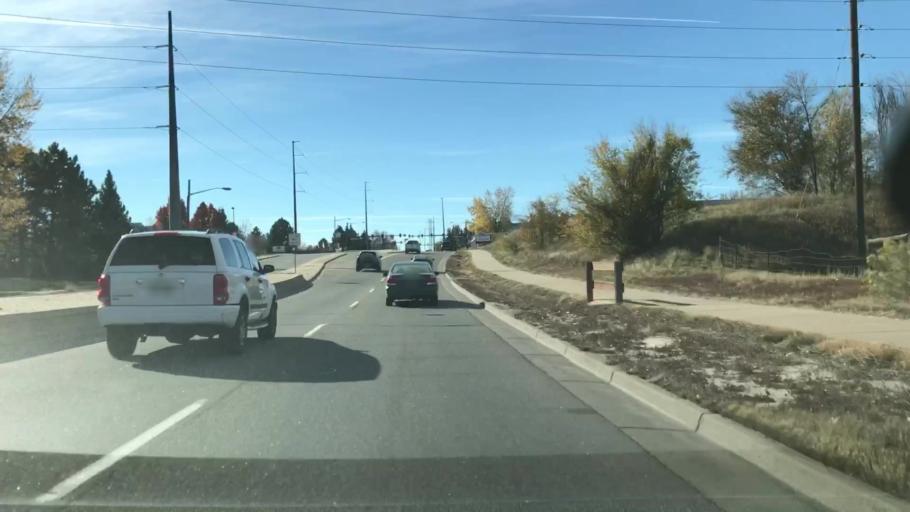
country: US
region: Colorado
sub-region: Arapahoe County
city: Glendale
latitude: 39.6805
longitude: -104.9036
